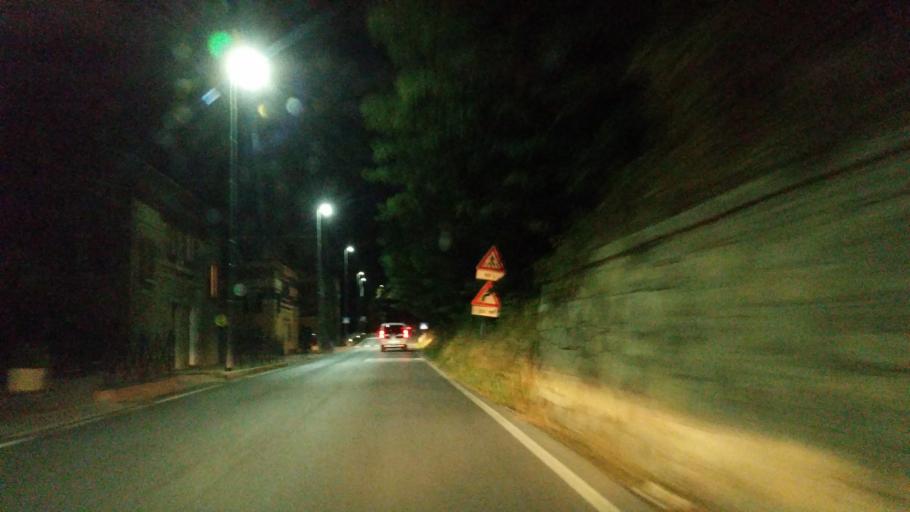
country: IT
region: Liguria
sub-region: Provincia di Savona
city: Cengio Alto
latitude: 44.3906
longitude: 8.1876
